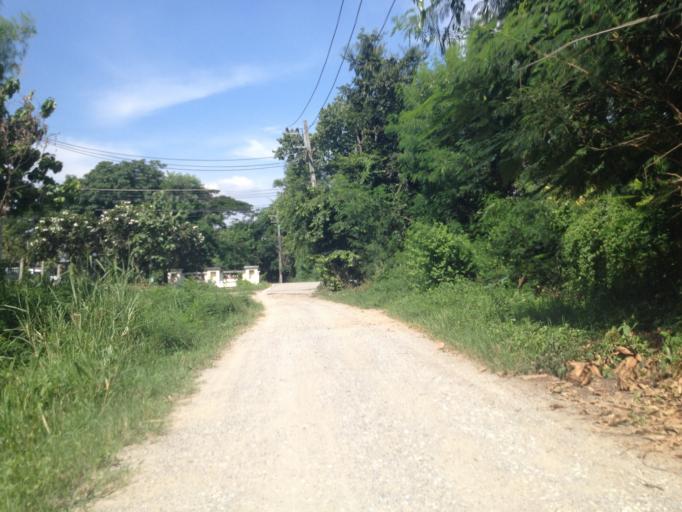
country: TH
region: Chiang Mai
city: Chiang Mai
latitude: 18.7569
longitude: 98.9439
